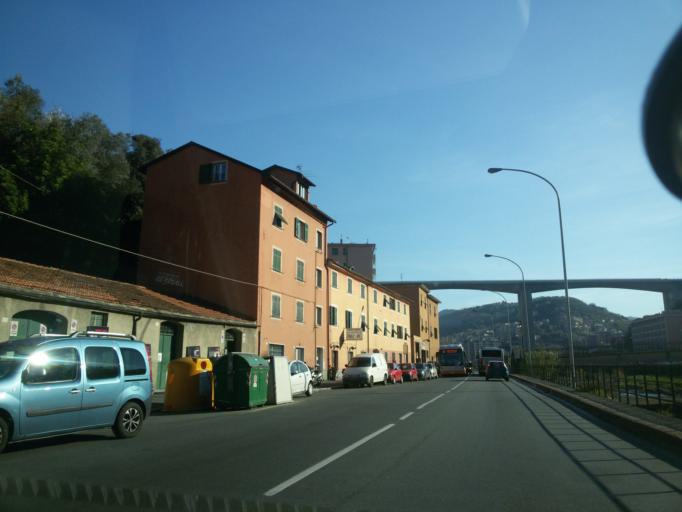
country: IT
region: Liguria
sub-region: Provincia di Genova
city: Genoa
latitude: 44.4298
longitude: 8.9561
